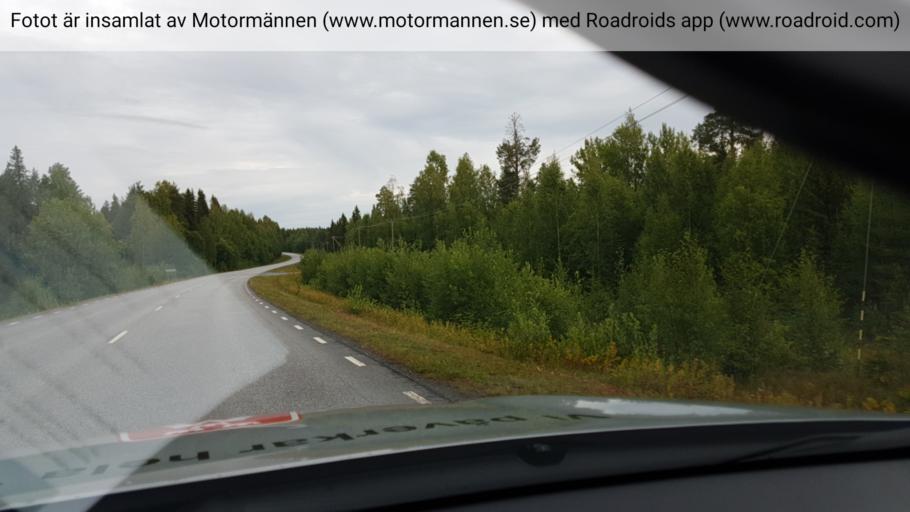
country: SE
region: Norrbotten
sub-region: Bodens Kommun
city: Boden
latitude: 65.8006
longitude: 21.6583
